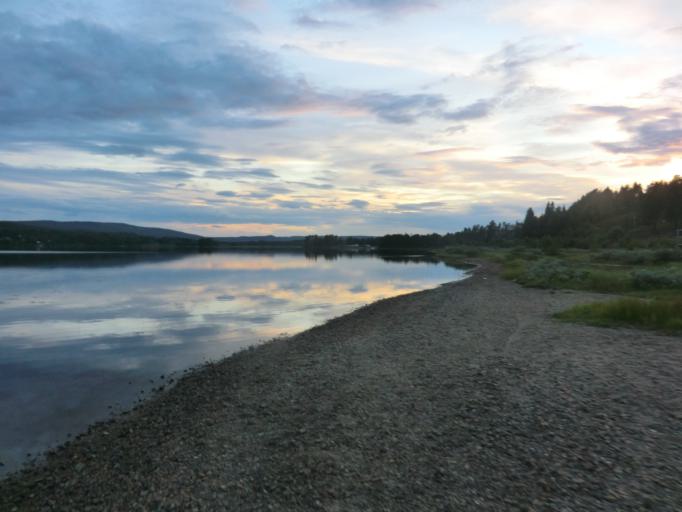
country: NO
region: Hedmark
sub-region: Trysil
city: Innbygda
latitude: 61.8524
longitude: 12.7473
